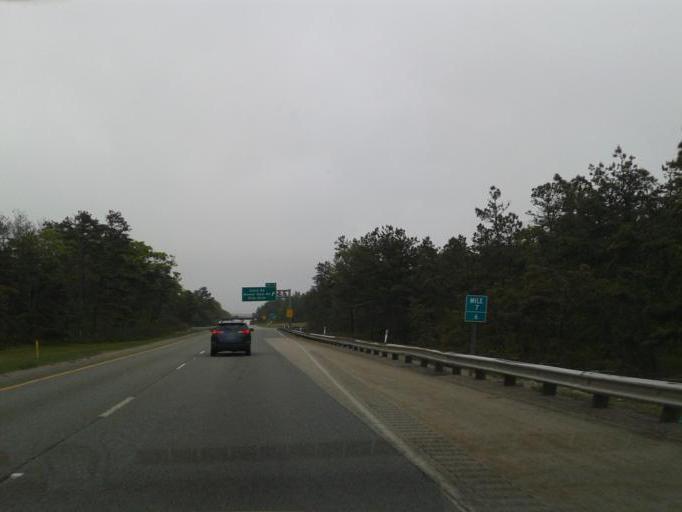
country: US
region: Massachusetts
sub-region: Plymouth County
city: White Island Shores
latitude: 41.8839
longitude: -70.6106
